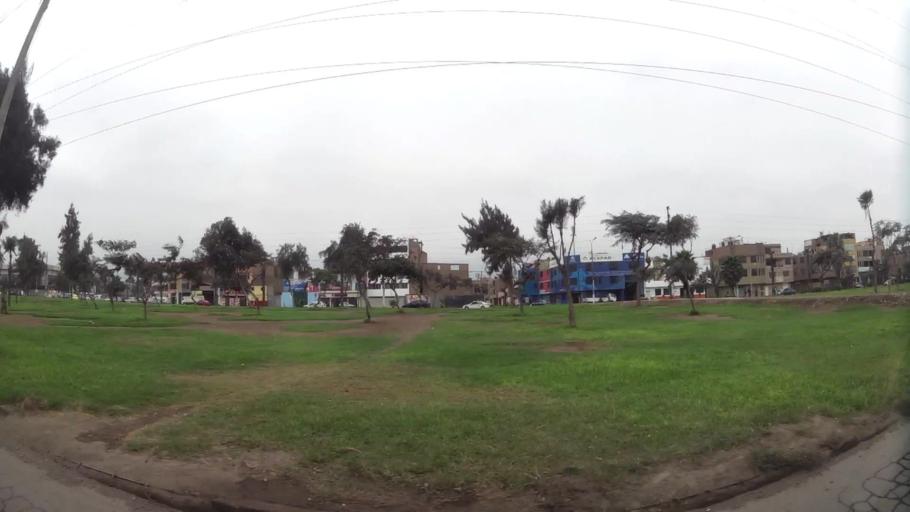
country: PE
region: Lima
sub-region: Lima
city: Independencia
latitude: -11.9794
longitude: -77.0779
